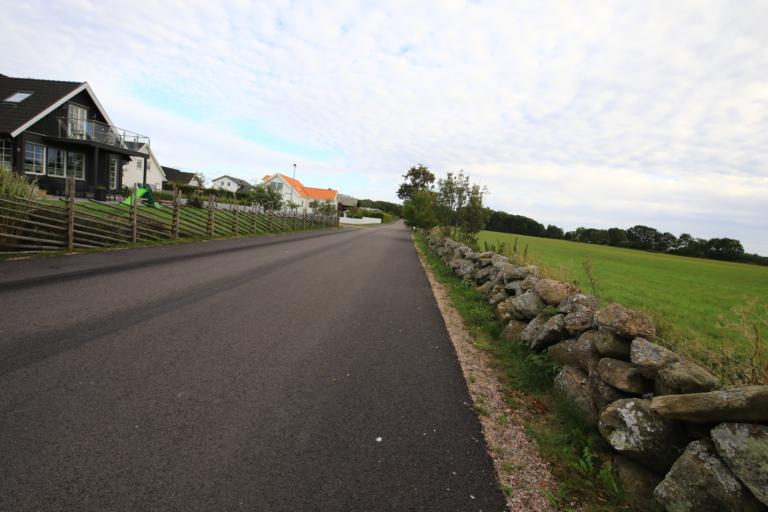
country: SE
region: Halland
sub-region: Varbergs Kommun
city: Varberg
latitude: 57.1452
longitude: 12.2313
